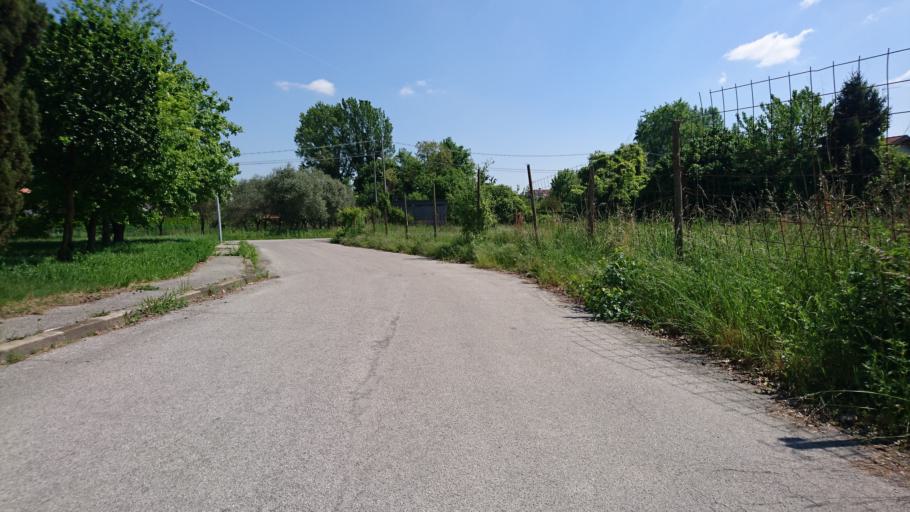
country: IT
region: Veneto
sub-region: Provincia di Padova
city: Padova
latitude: 45.4009
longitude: 11.9062
